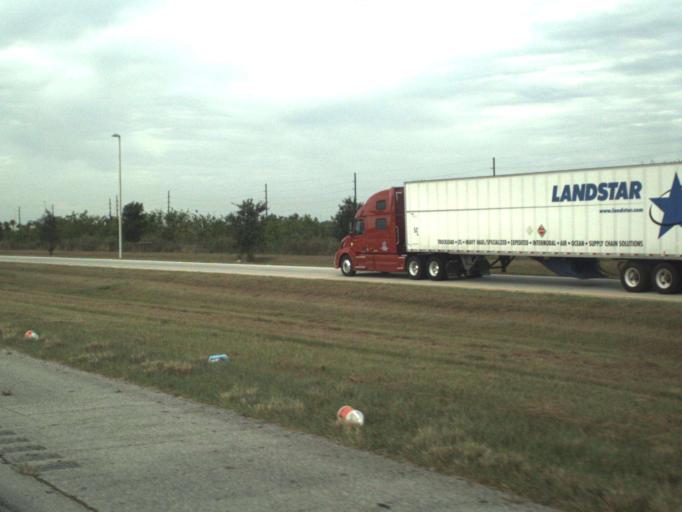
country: US
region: Florida
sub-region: Saint Lucie County
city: Port Saint Lucie
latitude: 27.1941
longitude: -80.4004
